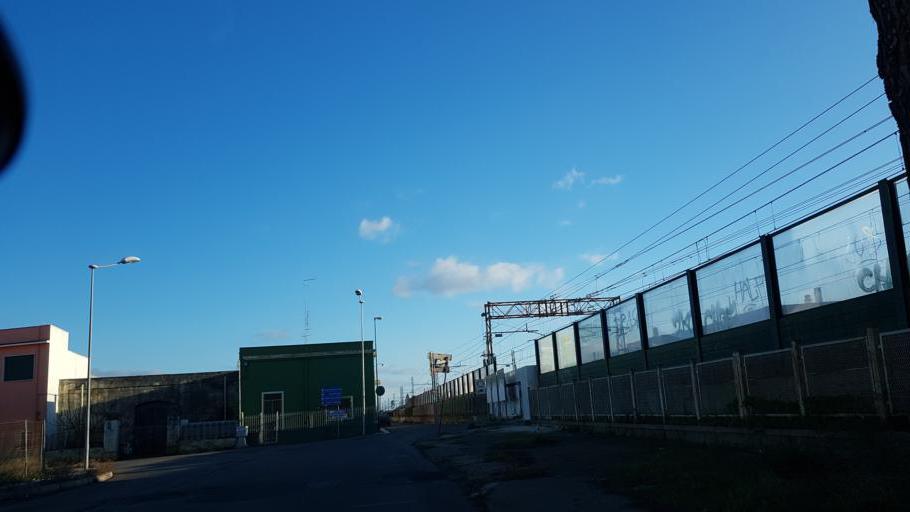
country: IT
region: Apulia
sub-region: Provincia di Lecce
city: Squinzano
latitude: 40.4343
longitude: 18.0516
